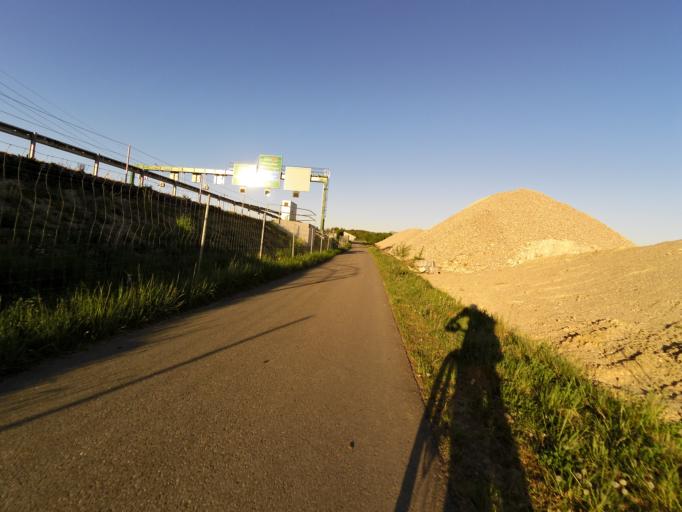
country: CH
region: Zurich
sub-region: Bezirk Winterthur
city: Oberwinterthur (Kreis 2)
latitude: 47.5280
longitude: 8.7652
